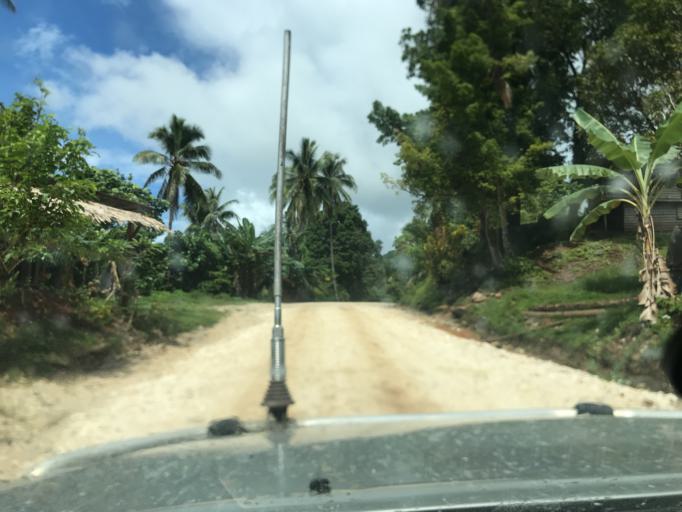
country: SB
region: Malaita
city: Auki
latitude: -8.4182
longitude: 160.8059
